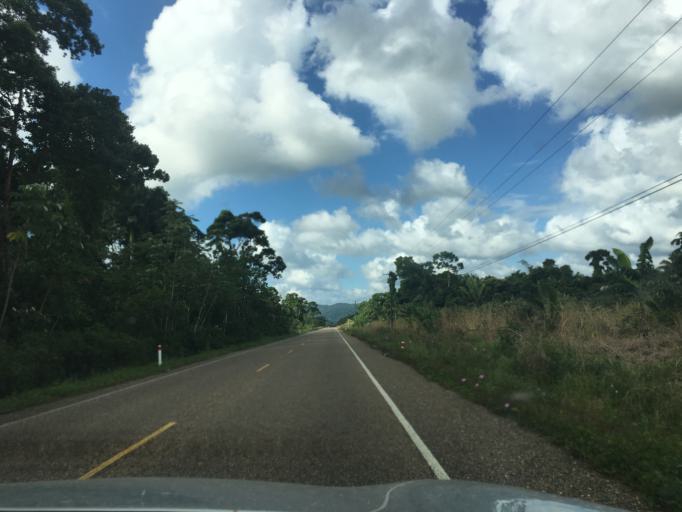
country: BZ
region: Stann Creek
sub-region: Dangriga
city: Dangriga
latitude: 16.8546
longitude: -88.3287
